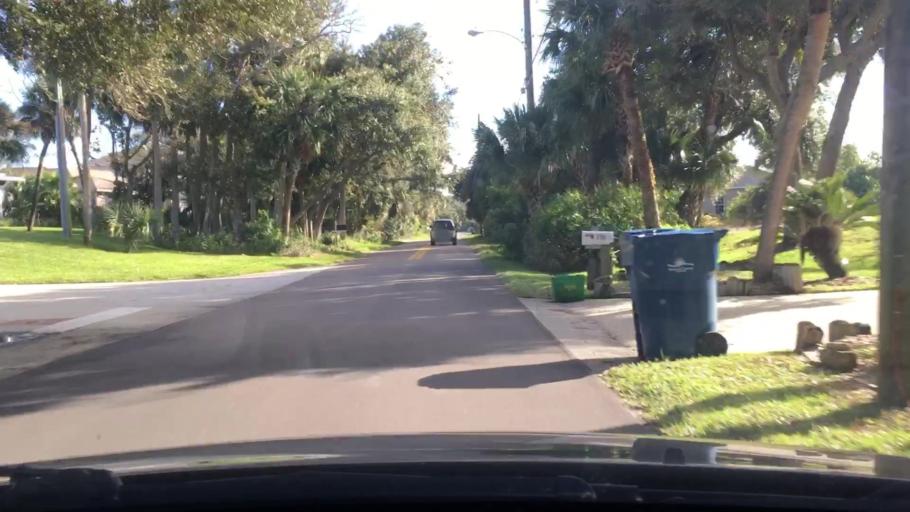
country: US
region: Florida
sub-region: Volusia County
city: Ormond-by-the-Sea
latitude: 29.3855
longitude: -81.0883
